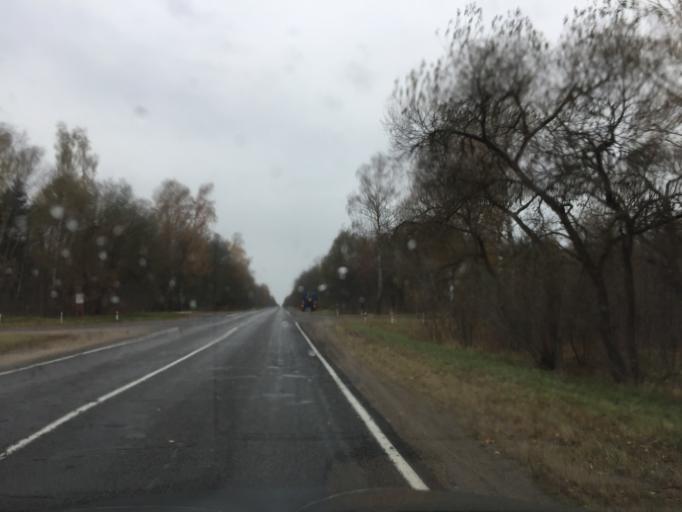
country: BY
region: Mogilev
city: Slawharad
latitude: 53.3672
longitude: 30.8551
